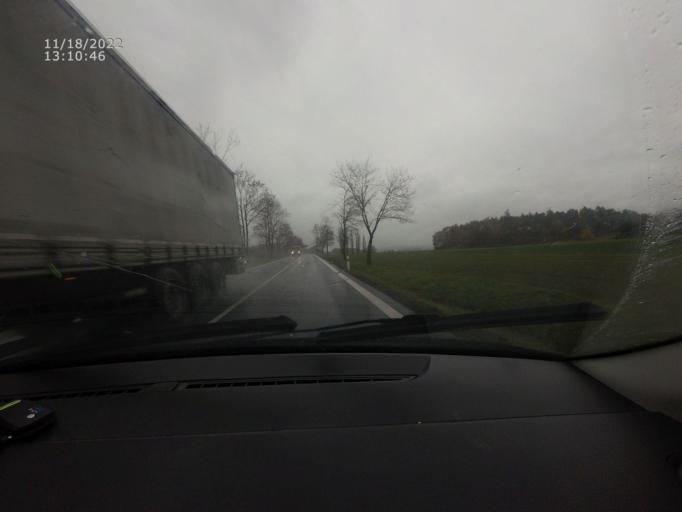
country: CZ
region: Plzensky
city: Hradek
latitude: 49.3302
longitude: 13.5690
